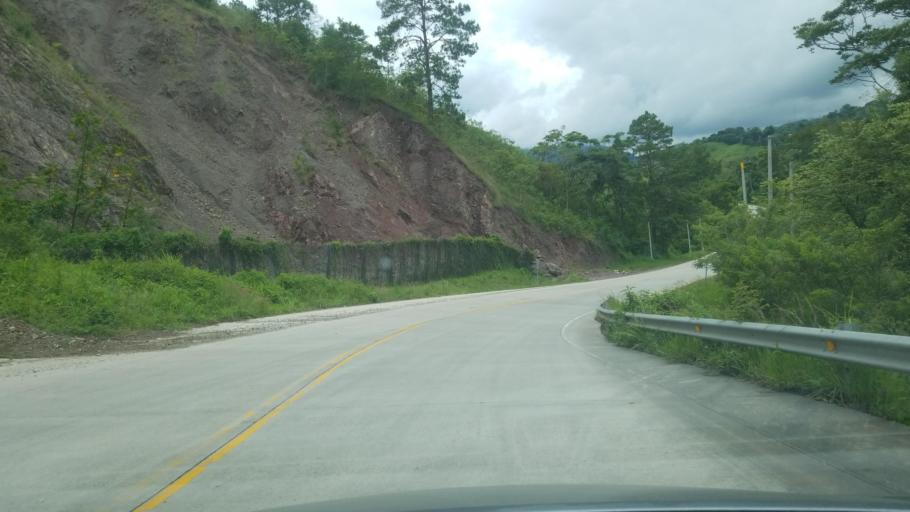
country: HN
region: Copan
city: San Jeronimo
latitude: 14.9650
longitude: -88.8942
